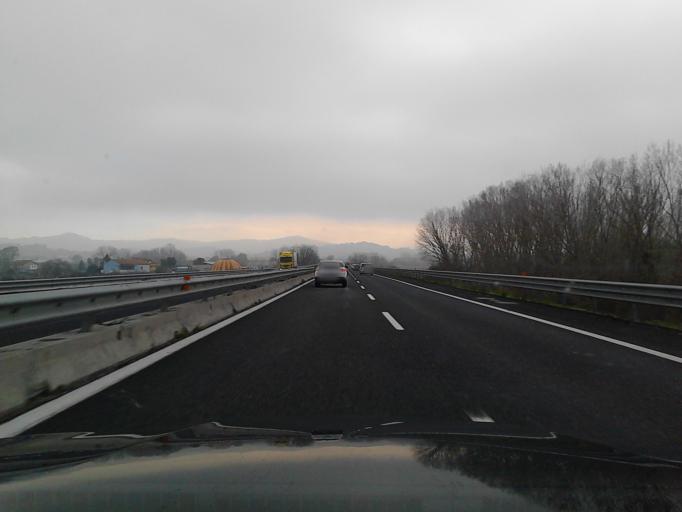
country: IT
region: Abruzzo
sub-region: Provincia di Pescara
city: Cappelle sul Tavo
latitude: 42.4964
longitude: 14.1148
